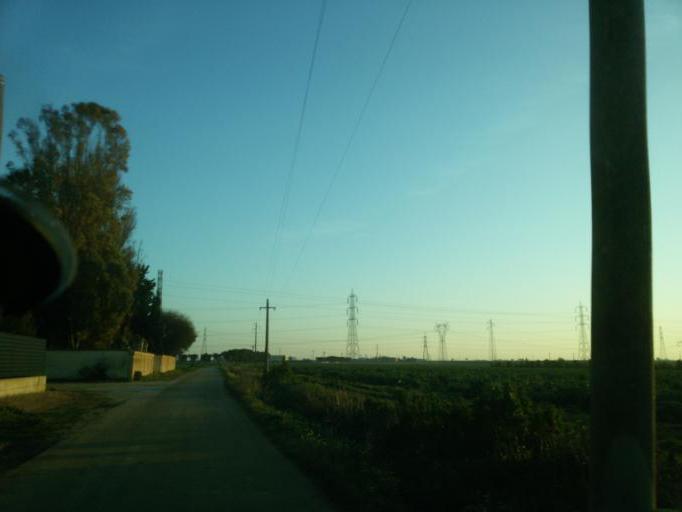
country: IT
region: Apulia
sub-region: Provincia di Brindisi
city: La Rosa
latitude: 40.6027
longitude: 17.9396
